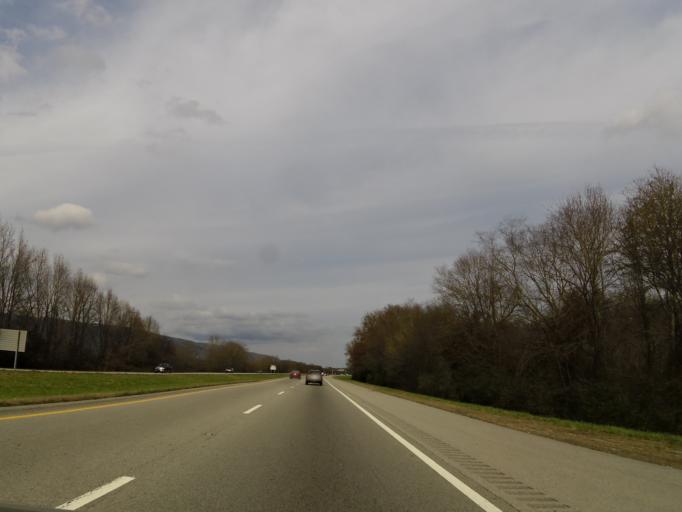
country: US
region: Tennessee
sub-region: Hamilton County
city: Falling Water
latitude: 35.2013
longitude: -85.2322
